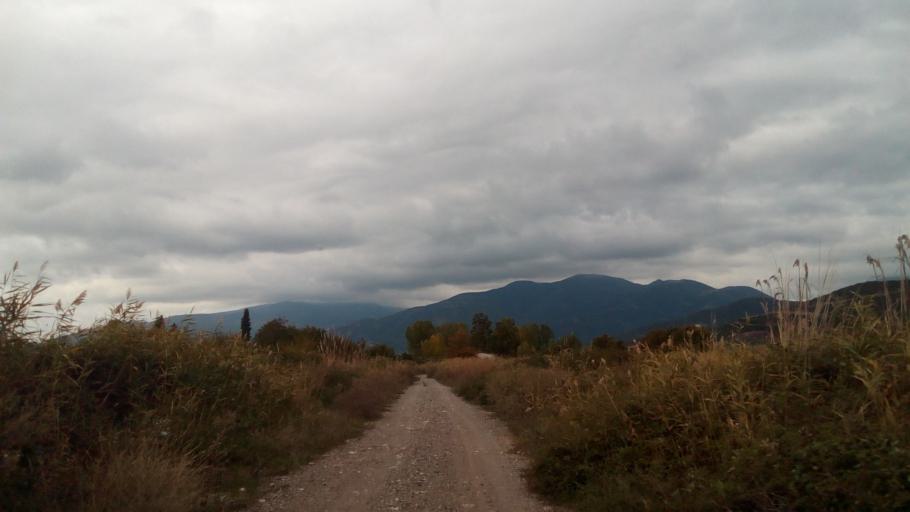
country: GR
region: West Greece
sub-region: Nomos Aitolias kai Akarnanias
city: Nafpaktos
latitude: 38.3955
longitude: 21.9179
